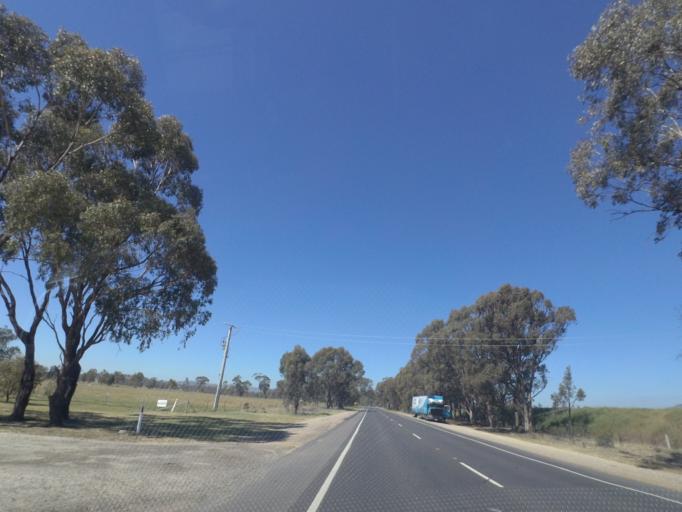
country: AU
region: Victoria
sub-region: Murrindindi
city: Kinglake West
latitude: -37.0297
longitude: 145.0814
